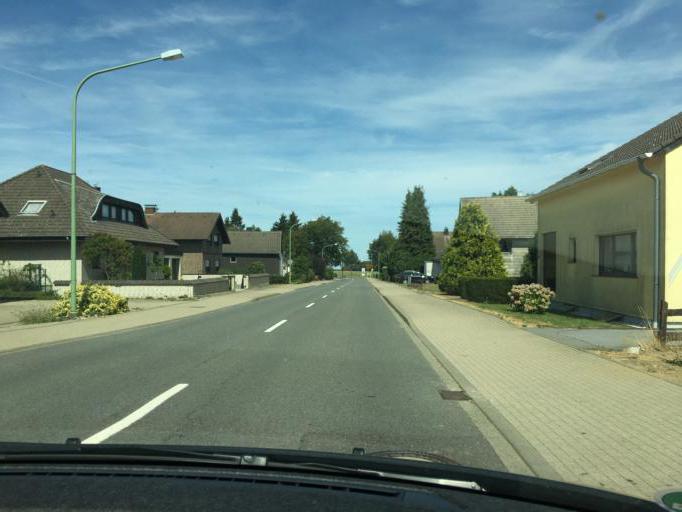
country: DE
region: North Rhine-Westphalia
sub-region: Regierungsbezirk Koln
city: Hurtgenwald
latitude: 50.6907
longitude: 6.3560
